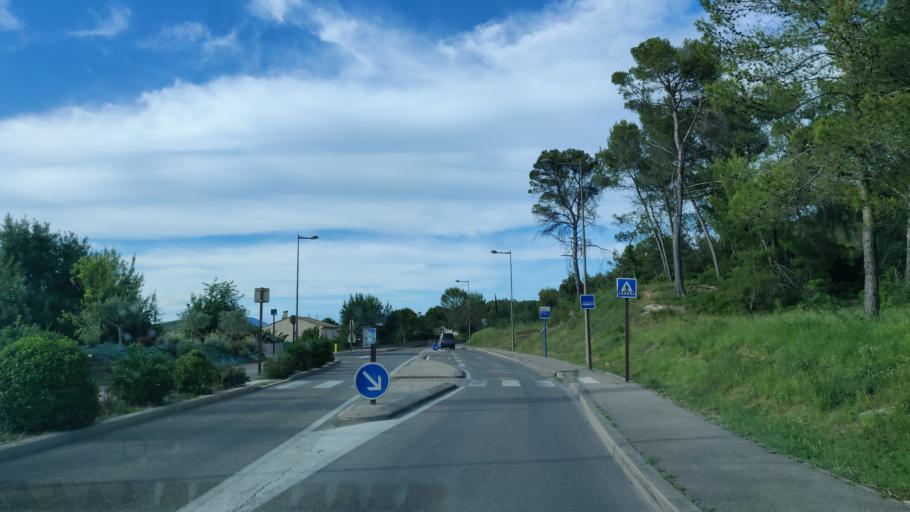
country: FR
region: Languedoc-Roussillon
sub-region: Departement de l'Herault
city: Grabels
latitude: 43.6539
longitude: 3.7901
